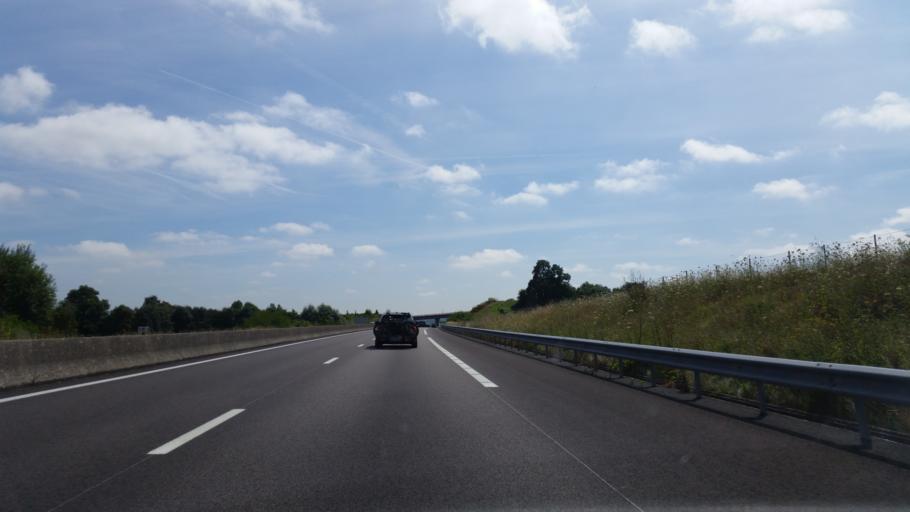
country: FR
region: Haute-Normandie
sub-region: Departement de la Seine-Maritime
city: Neufchatel-en-Bray
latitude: 49.7463
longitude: 1.5238
